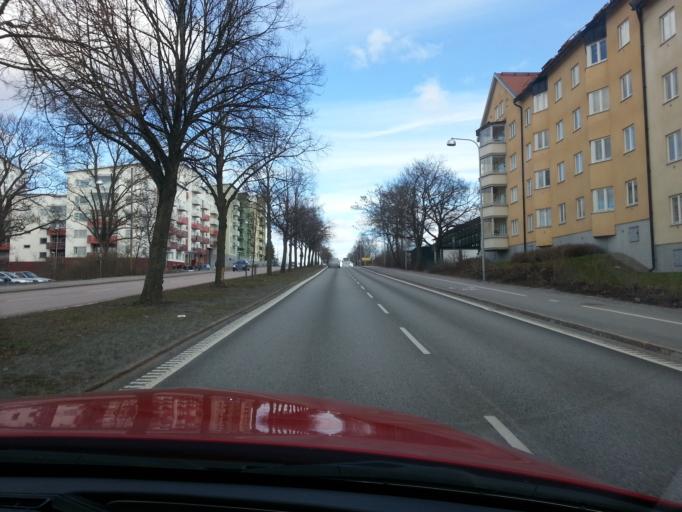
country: SE
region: Uppsala
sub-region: Uppsala Kommun
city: Uppsala
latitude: 59.8721
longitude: 17.6684
